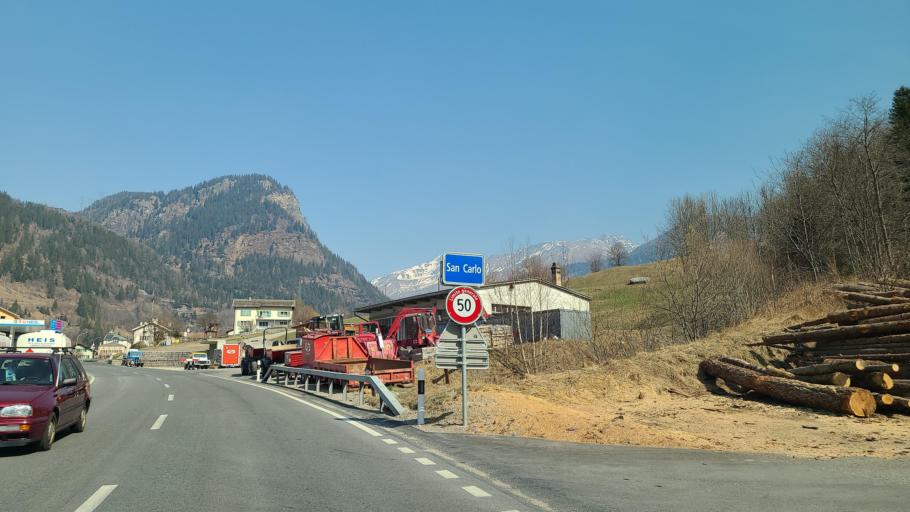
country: CH
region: Grisons
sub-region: Bernina District
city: Poschiavo
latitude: 46.3369
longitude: 10.0614
